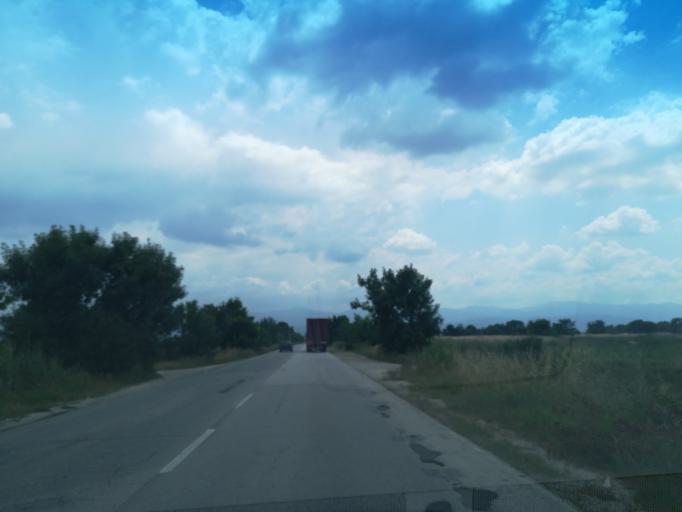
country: BG
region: Plovdiv
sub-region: Obshtina Plovdiv
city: Plovdiv
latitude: 42.1804
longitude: 24.6765
